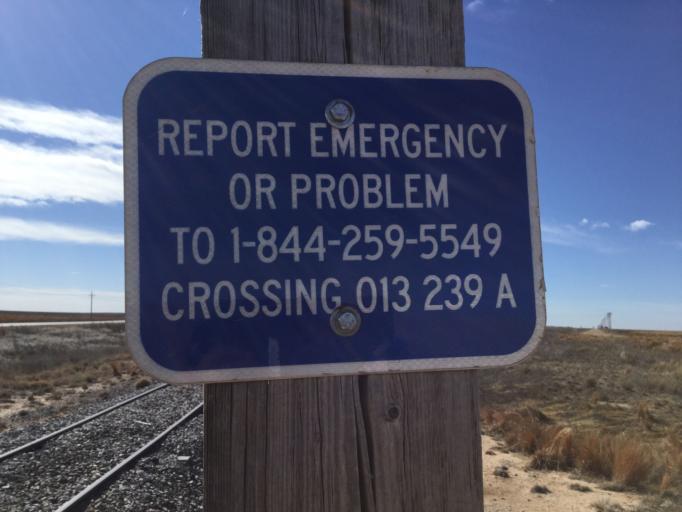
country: US
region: Kansas
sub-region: Morton County
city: Elkhart
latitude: 37.1127
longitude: -101.6697
